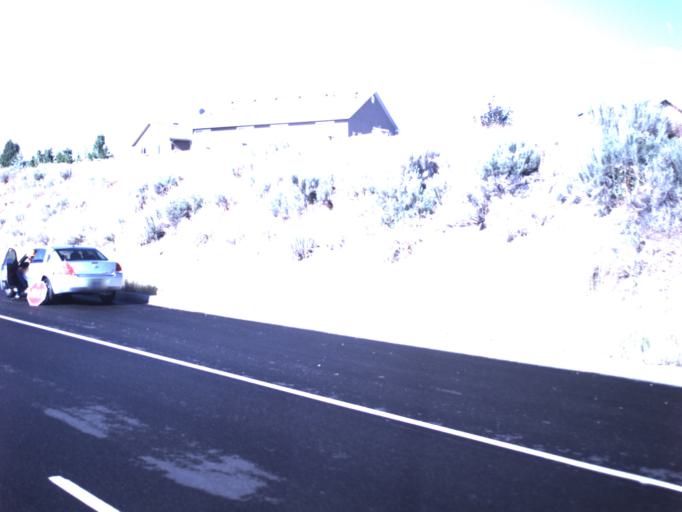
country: US
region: Utah
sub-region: Salt Lake County
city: Oquirrh
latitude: 40.6081
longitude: -112.0559
